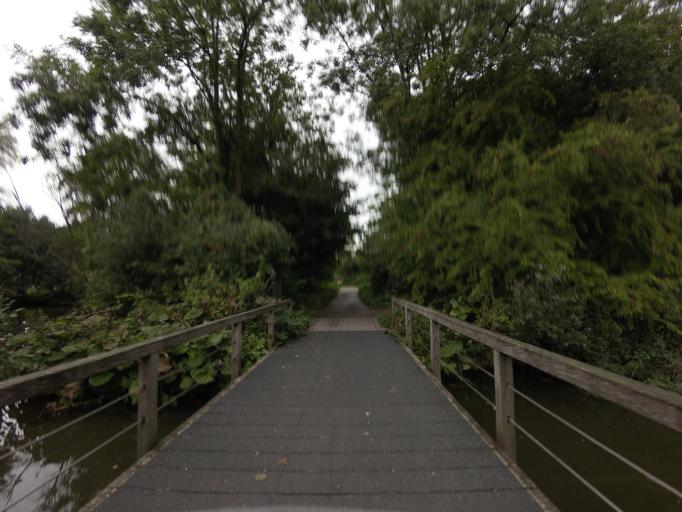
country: NL
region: Friesland
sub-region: Gemeente Leeuwarden
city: Bilgaard
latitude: 53.2174
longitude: 5.7918
